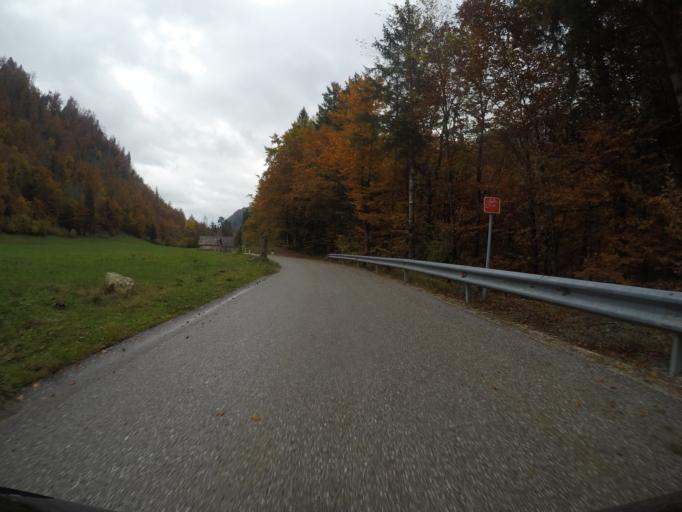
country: SI
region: Gorje
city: Zgornje Gorje
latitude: 46.3897
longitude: 14.0247
